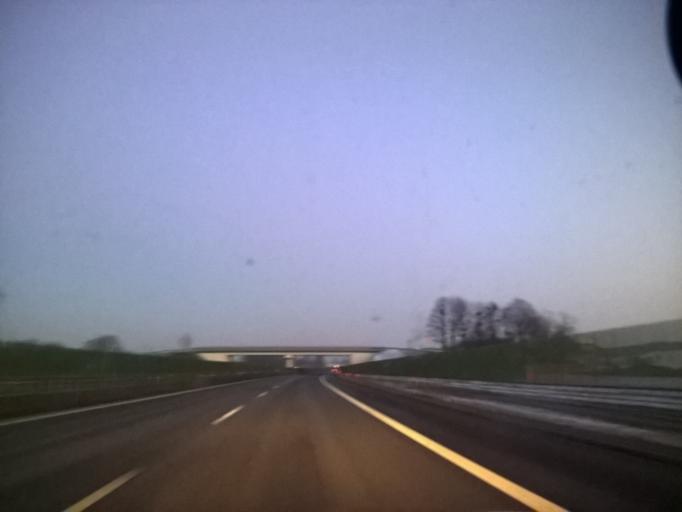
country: PL
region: Warmian-Masurian Voivodeship
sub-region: Powiat olsztynski
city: Biskupiec
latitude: 53.8397
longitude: 21.0144
